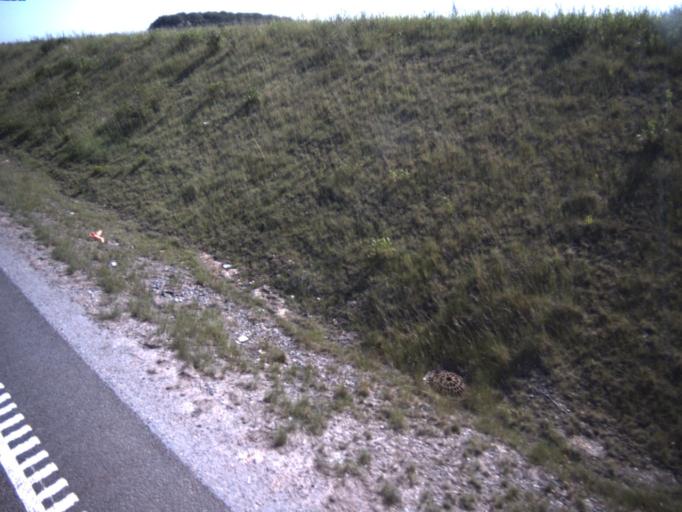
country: SE
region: Skane
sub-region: Helsingborg
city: Helsingborg
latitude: 56.0373
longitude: 12.7592
